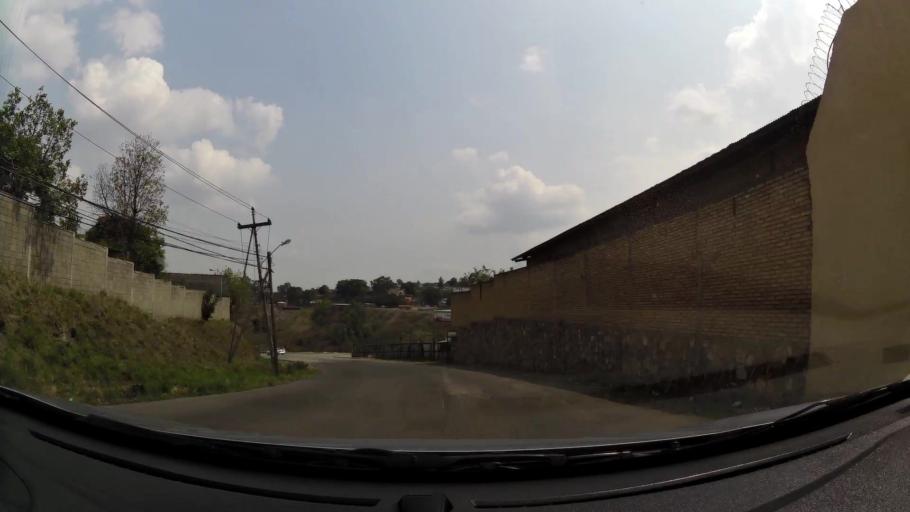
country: HN
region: Francisco Morazan
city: El Lolo
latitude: 14.1223
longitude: -87.2236
